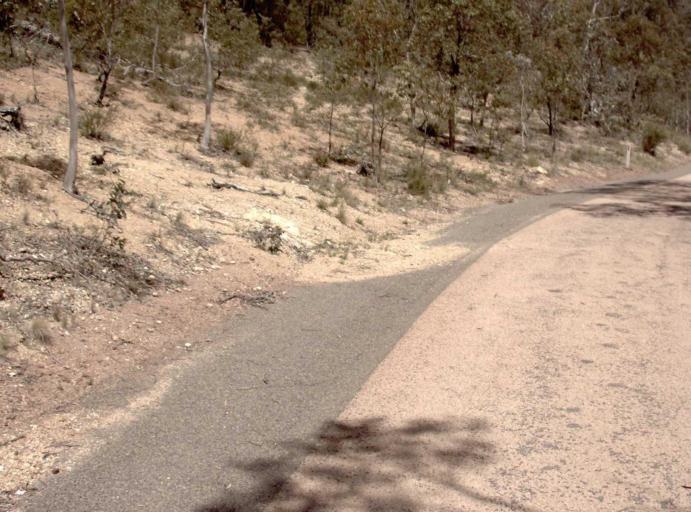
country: AU
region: New South Wales
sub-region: Snowy River
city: Jindabyne
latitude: -37.0641
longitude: 148.2979
